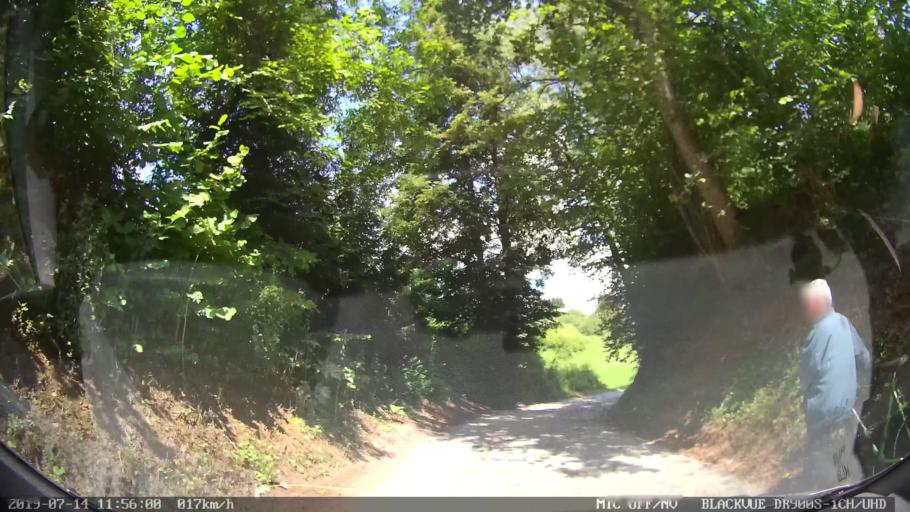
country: HR
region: Karlovacka
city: Vojnic
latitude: 45.3851
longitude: 15.6066
